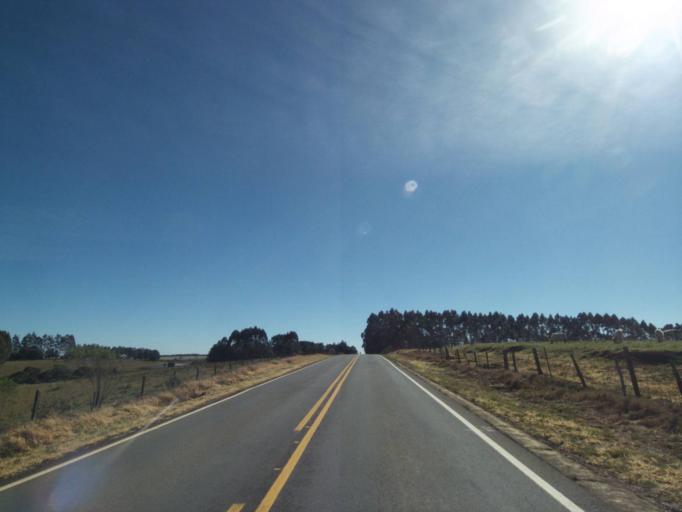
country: BR
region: Parana
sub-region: Castro
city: Castro
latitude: -24.7182
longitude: -50.1890
